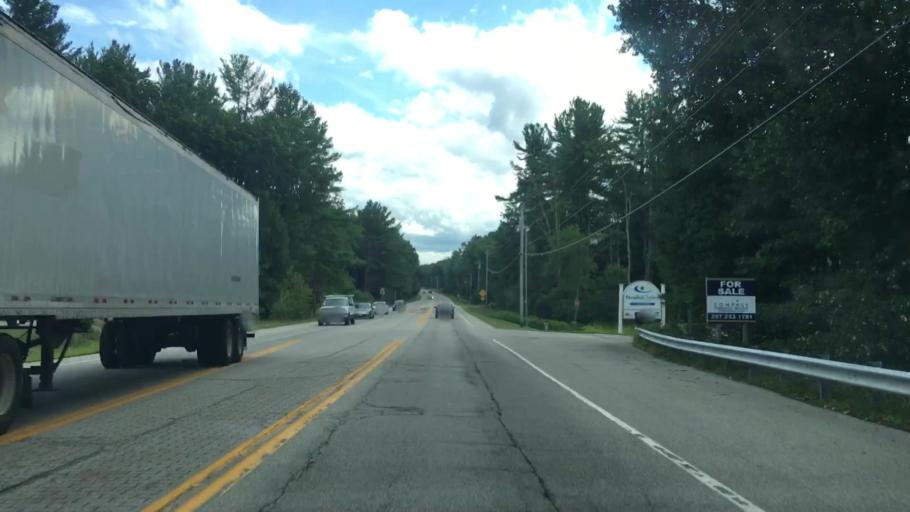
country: US
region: Maine
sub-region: York County
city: South Sanford
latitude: 43.4088
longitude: -70.7425
